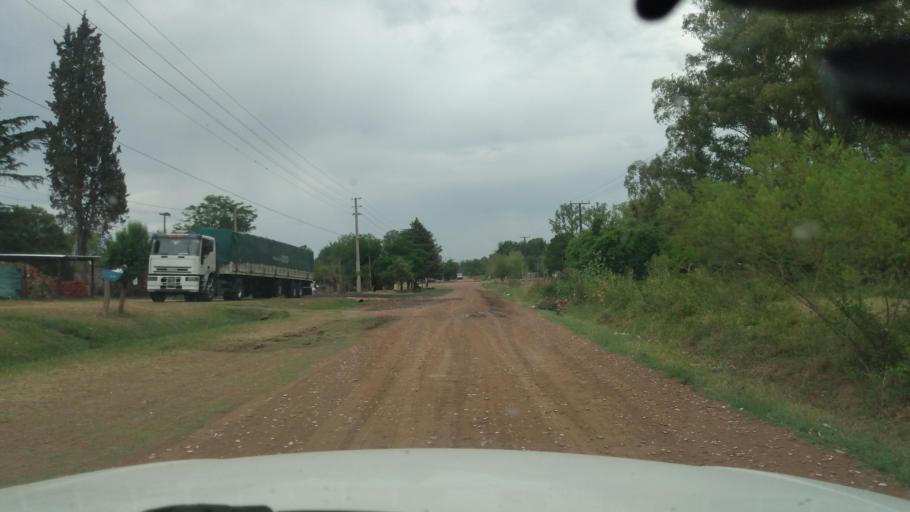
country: AR
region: Buenos Aires
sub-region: Partido de Lujan
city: Lujan
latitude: -34.5602
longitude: -59.1873
